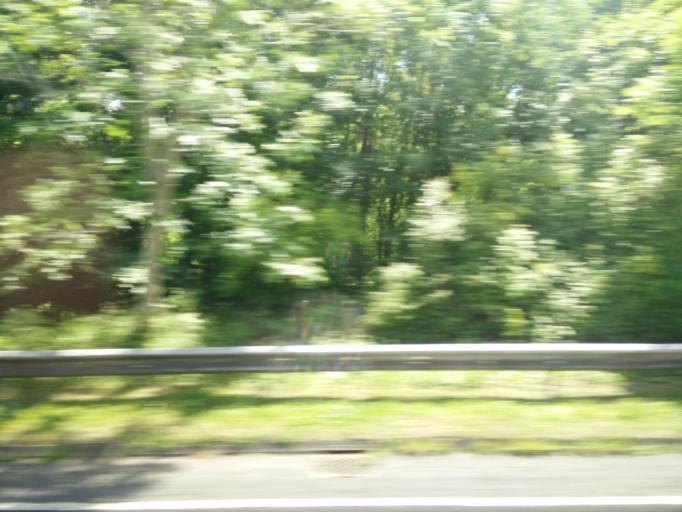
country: GB
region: England
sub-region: Hertfordshire
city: Hitchin
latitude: 51.9345
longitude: -0.3347
